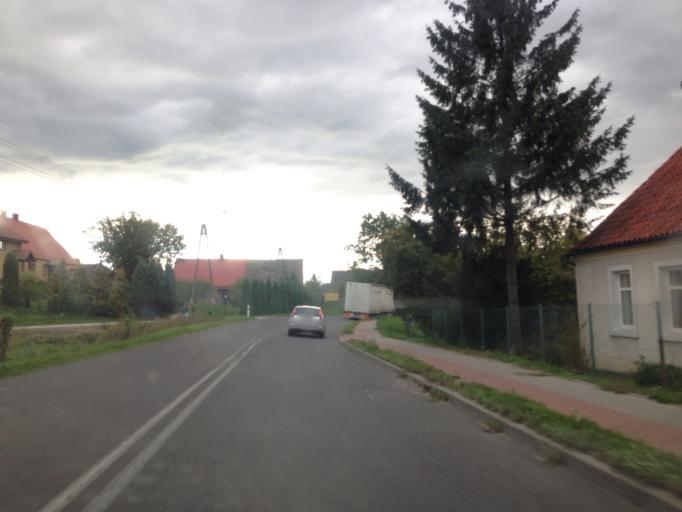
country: PL
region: Pomeranian Voivodeship
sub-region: Powiat kwidzynski
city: Kwidzyn
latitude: 53.7266
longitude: 19.0179
